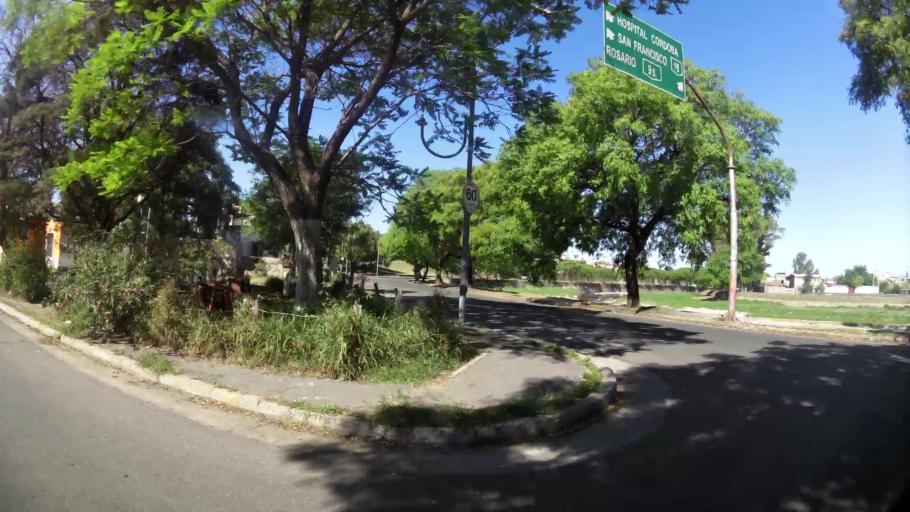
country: AR
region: Cordoba
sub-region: Departamento de Capital
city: Cordoba
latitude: -31.4164
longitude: -64.1574
